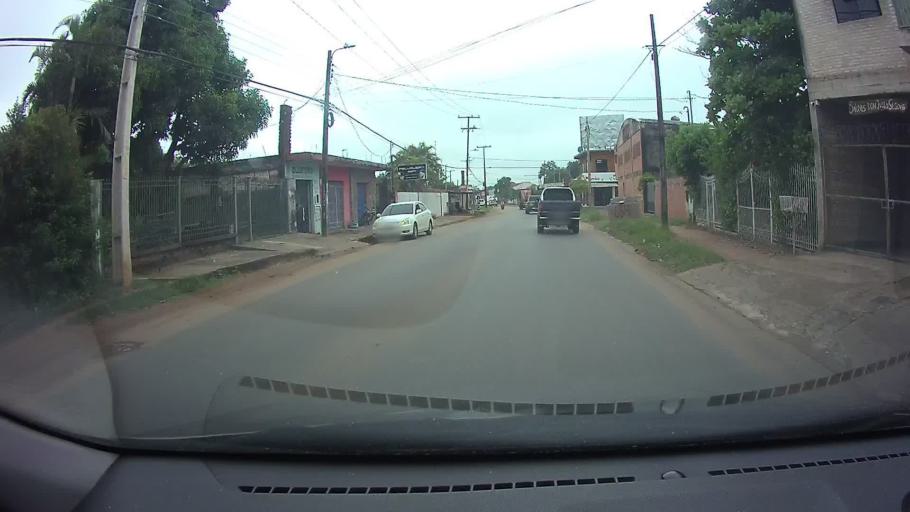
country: PY
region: Central
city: San Lorenzo
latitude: -25.3317
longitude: -57.5051
